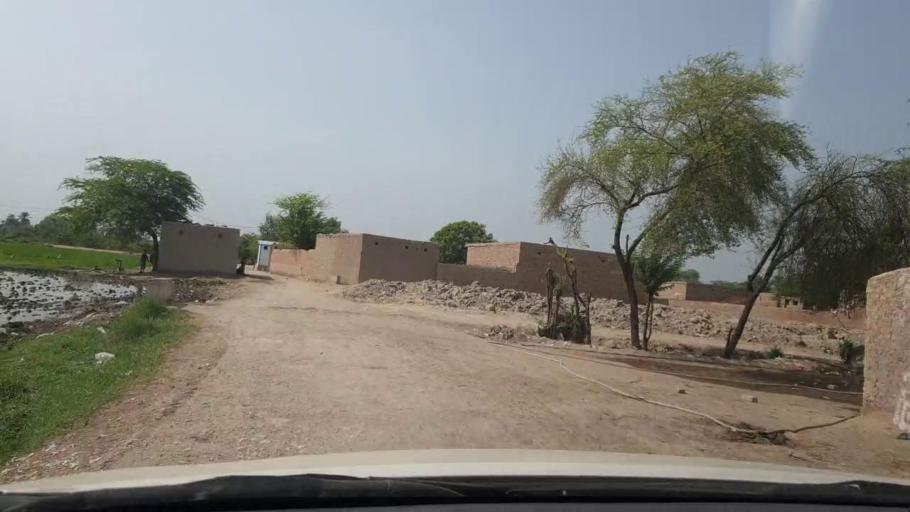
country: PK
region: Sindh
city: Shikarpur
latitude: 27.9807
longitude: 68.6737
